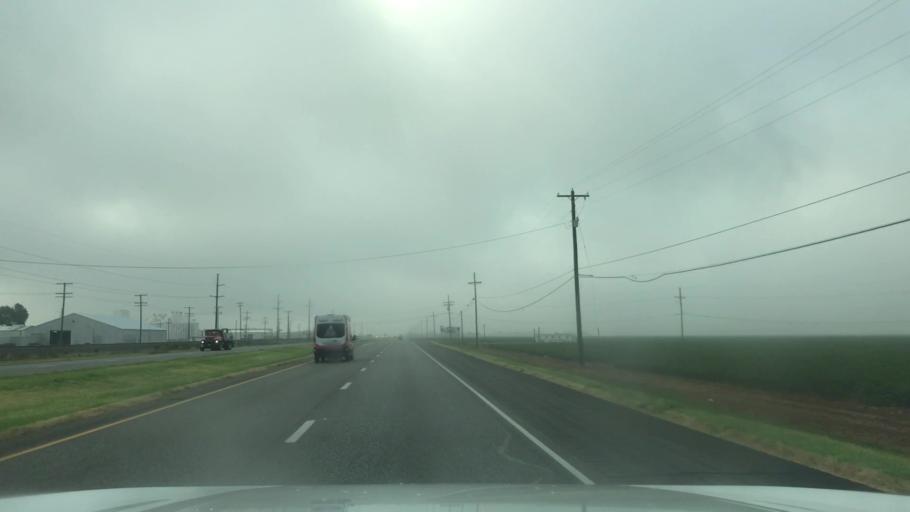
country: US
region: Texas
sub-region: Lubbock County
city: Ransom Canyon
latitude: 33.5069
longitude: -101.7544
